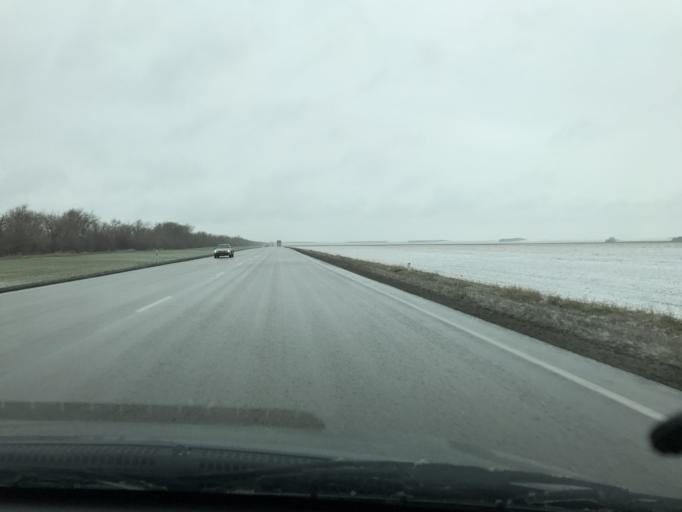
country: RU
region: Rostov
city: Kagal'nitskaya
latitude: 46.9218
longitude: 40.1035
